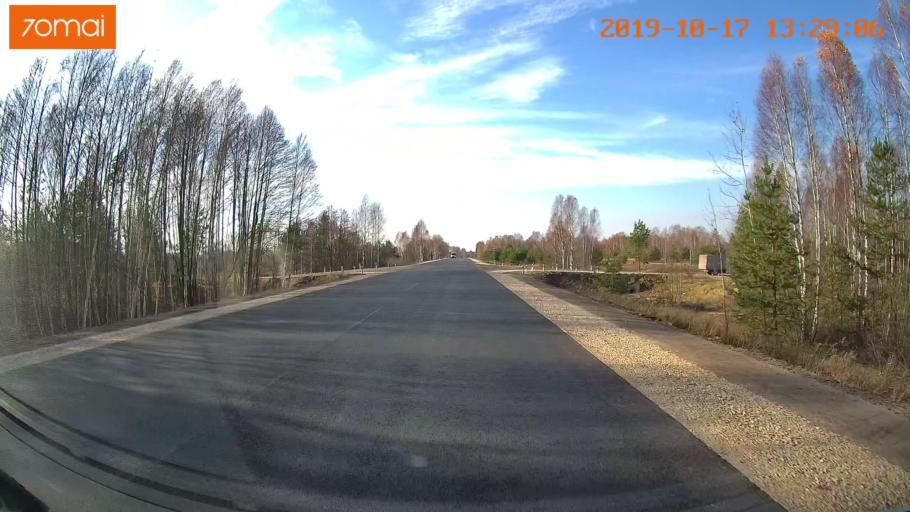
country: RU
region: Vladimir
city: Velikodvorskiy
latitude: 55.1183
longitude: 40.8499
